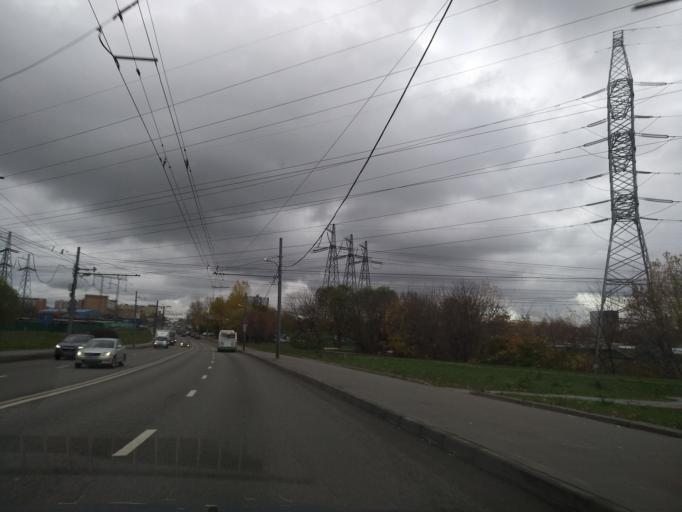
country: RU
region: Moscow
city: Kozeyevo
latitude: 55.8901
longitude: 37.6243
